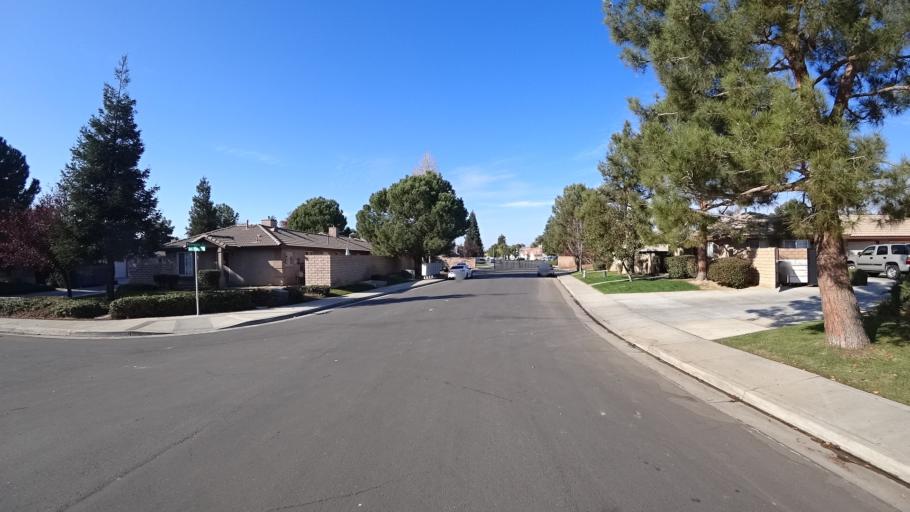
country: US
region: California
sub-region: Kern County
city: Greenacres
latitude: 35.4053
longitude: -119.0939
